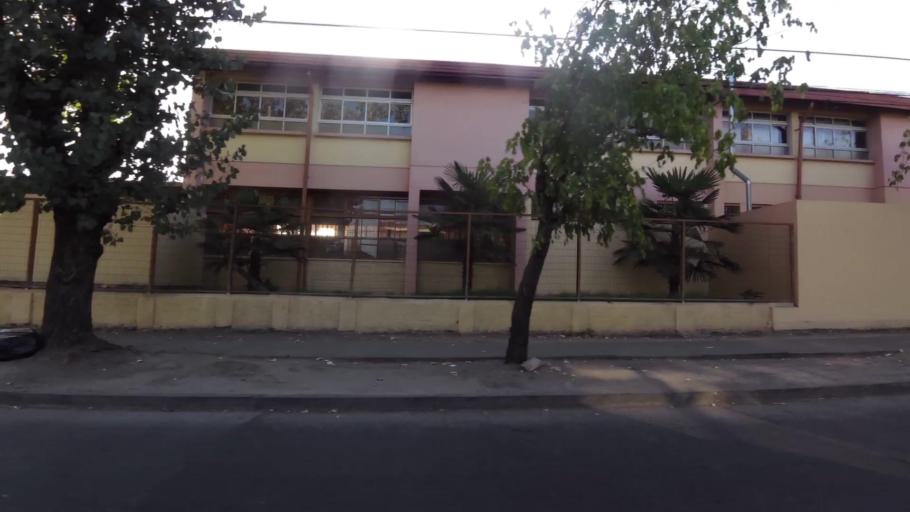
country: CL
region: Maule
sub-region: Provincia de Talca
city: Talca
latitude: -35.4363
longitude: -71.6461
